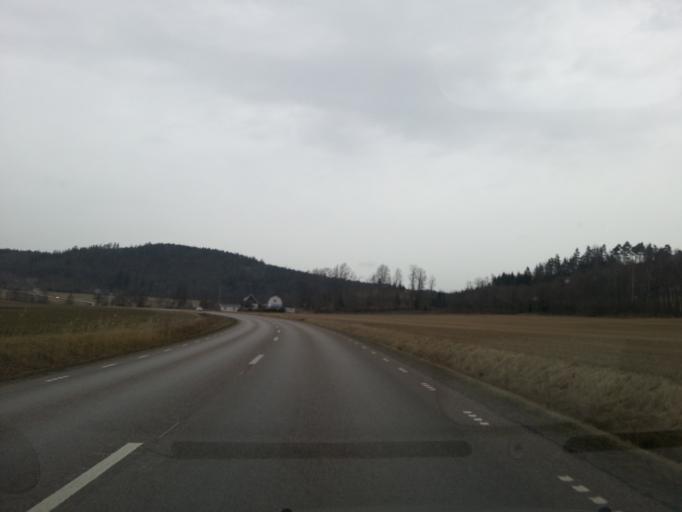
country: SE
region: Vaestra Goetaland
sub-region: Lilla Edets Kommun
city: Lilla Edet
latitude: 58.1389
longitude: 12.0991
